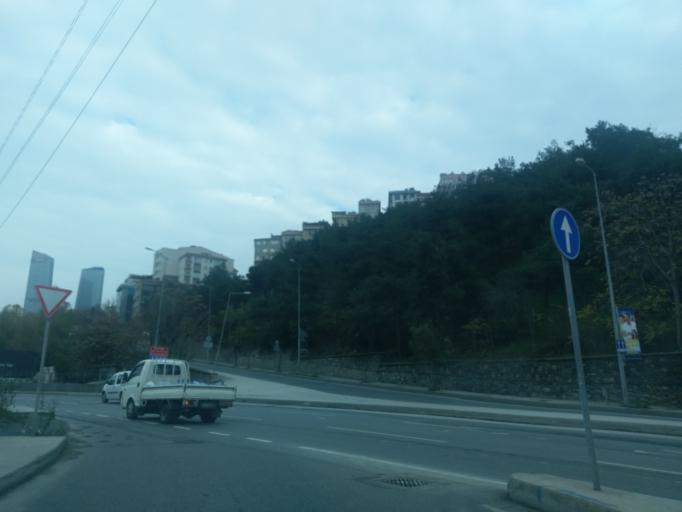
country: TR
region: Istanbul
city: Sisli
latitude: 41.0912
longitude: 28.9850
